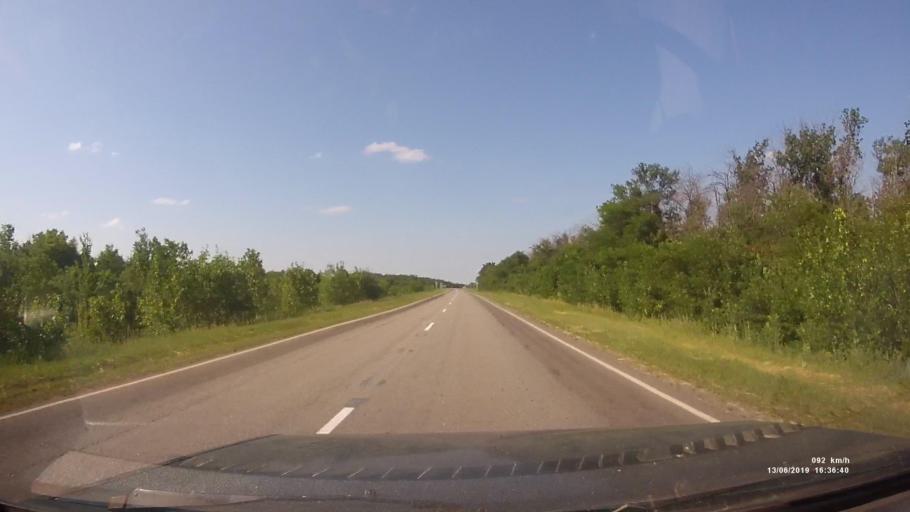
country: RU
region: Rostov
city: Kazanskaya
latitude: 49.8979
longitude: 41.3076
